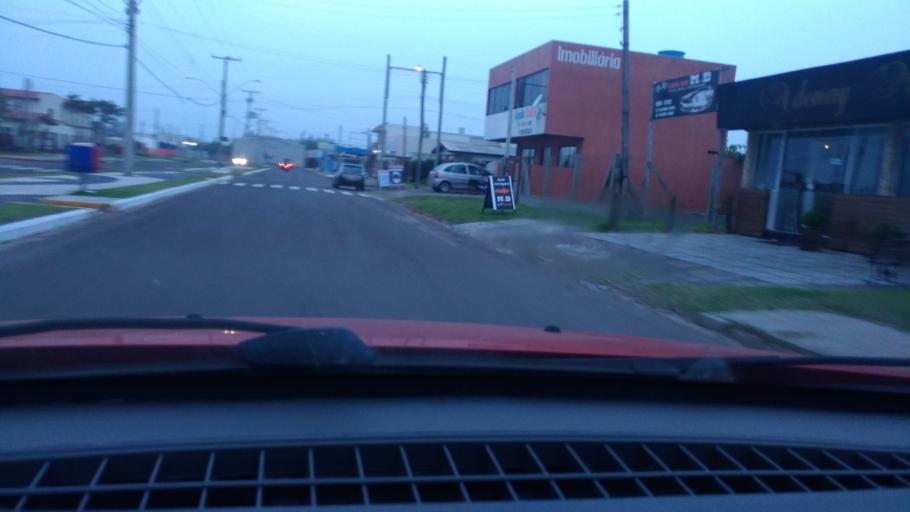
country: BR
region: Rio Grande do Sul
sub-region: Capao Da Canoa
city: Capao da Canoa
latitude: -29.8525
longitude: -50.0677
